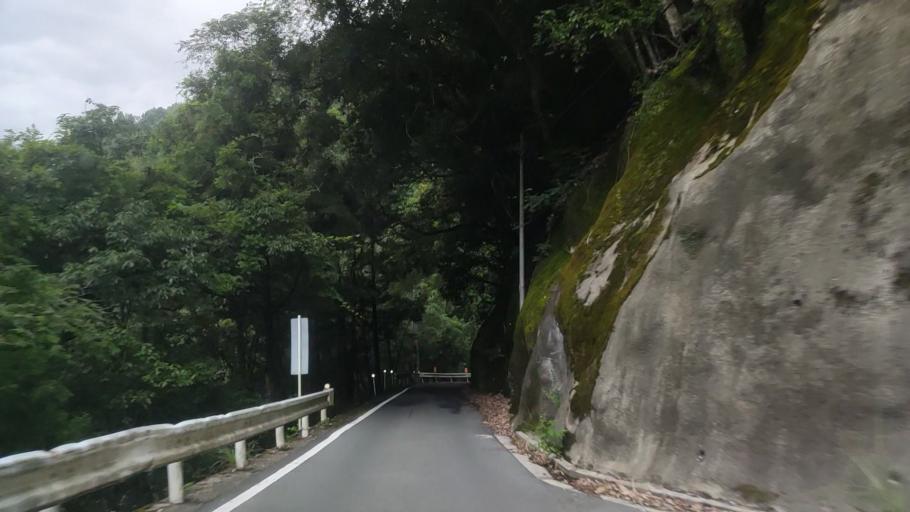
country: JP
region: Wakayama
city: Hashimoto
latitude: 34.2706
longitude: 135.6391
